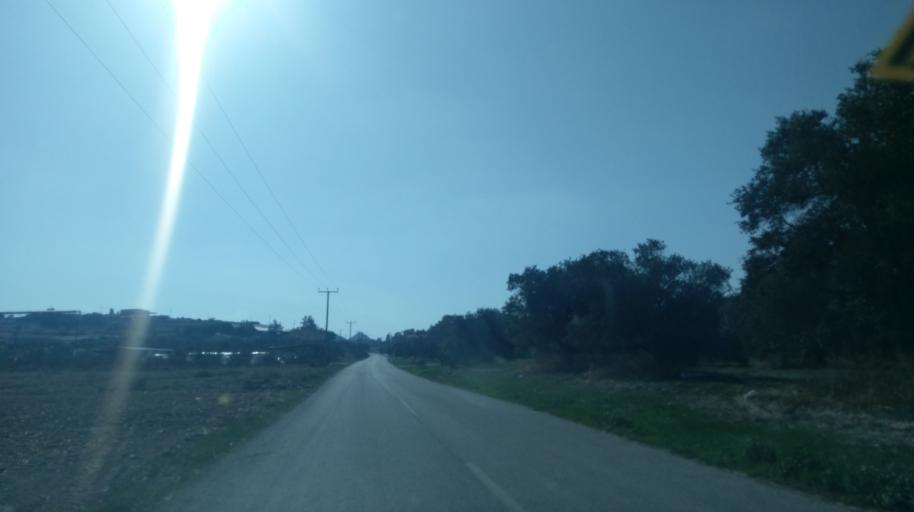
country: CY
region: Lefkosia
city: Lympia
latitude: 35.0228
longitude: 33.4688
